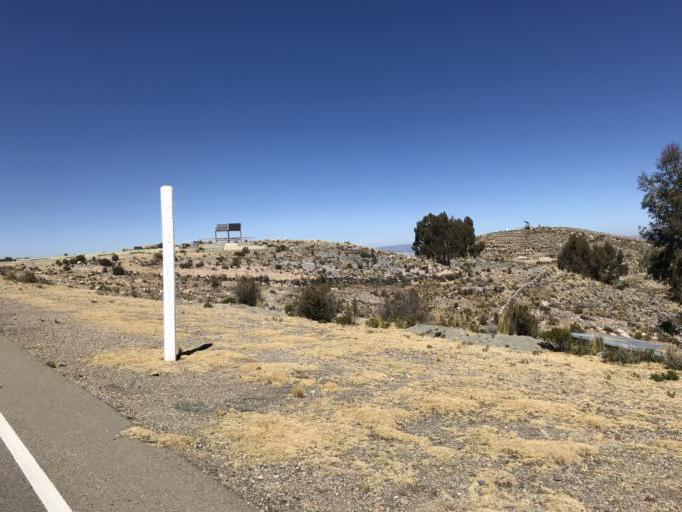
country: BO
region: La Paz
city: San Pedro
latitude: -16.2002
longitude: -68.9085
